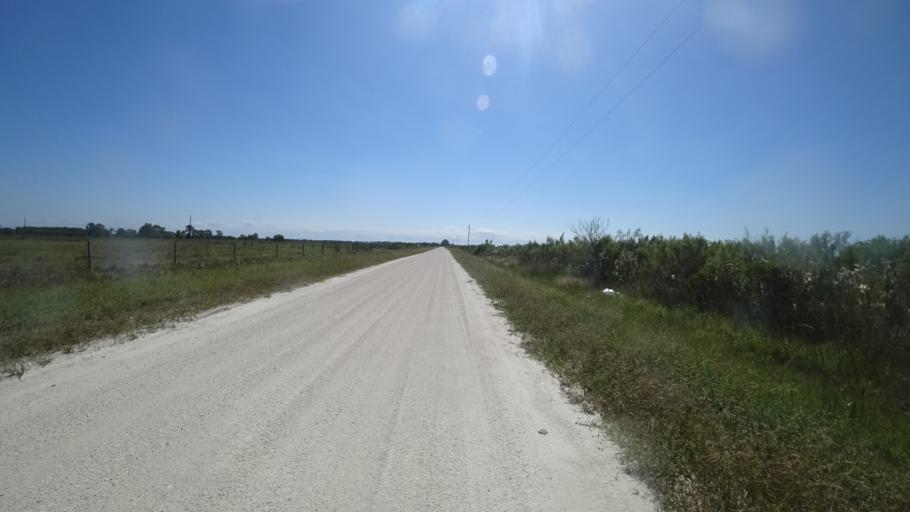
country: US
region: Florida
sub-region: DeSoto County
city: Arcadia
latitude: 27.3377
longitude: -82.0806
